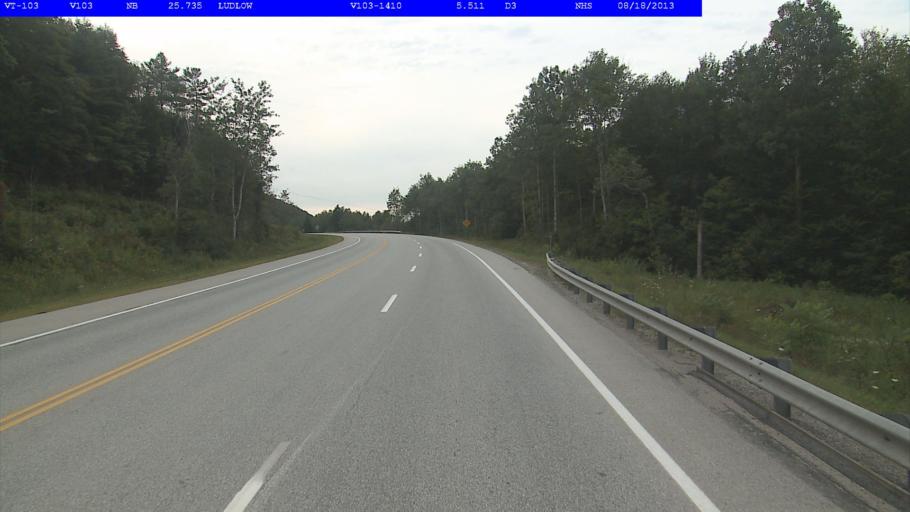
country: US
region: Vermont
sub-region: Windsor County
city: Chester
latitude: 43.4342
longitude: -72.7278
